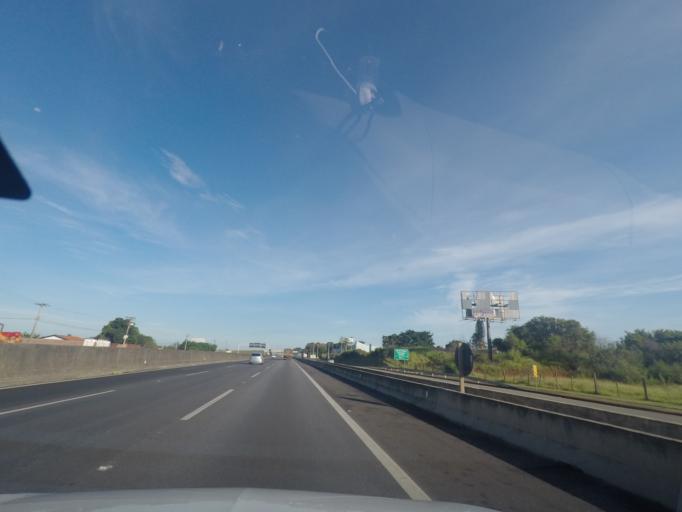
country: BR
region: Sao Paulo
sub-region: Nova Odessa
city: Nova Odessa
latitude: -22.7581
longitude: -47.2532
